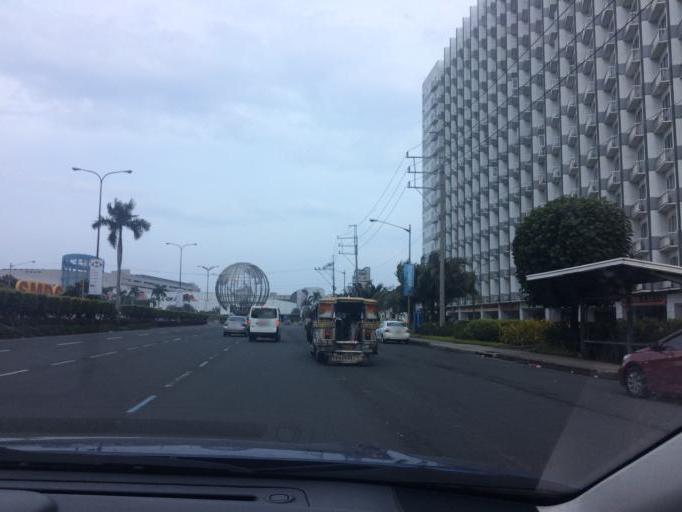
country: PH
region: Metro Manila
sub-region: Makati City
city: Makati City
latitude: 14.5359
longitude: 120.9869
